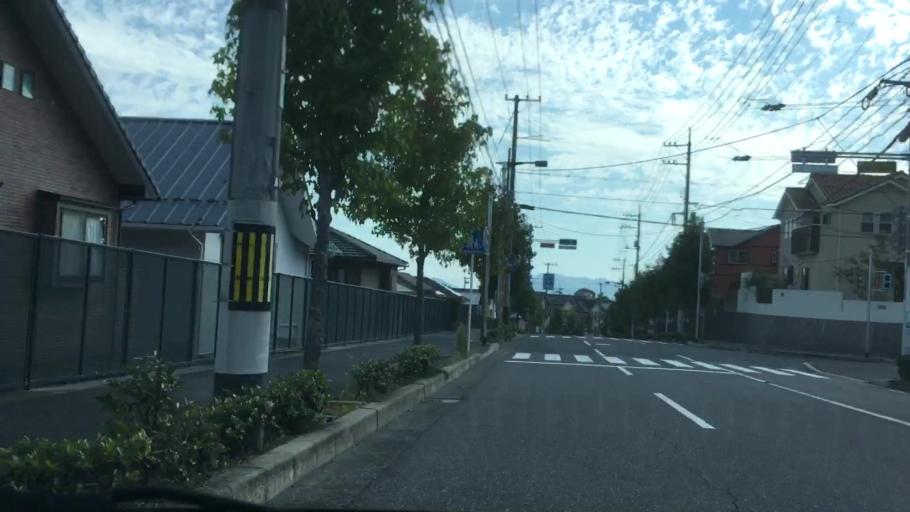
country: JP
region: Hiroshima
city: Hiroshima-shi
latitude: 34.3989
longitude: 132.4177
